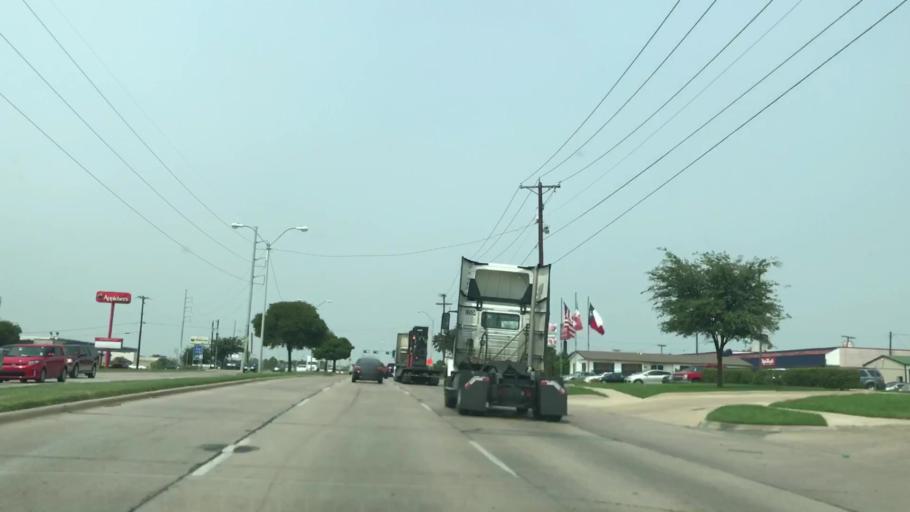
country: US
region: Texas
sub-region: Dallas County
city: Irving
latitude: 32.8330
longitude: -96.9936
